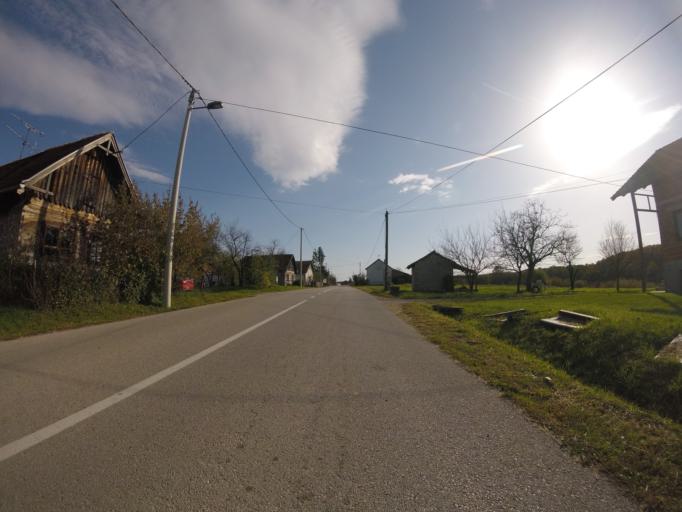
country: HR
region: Zagrebacka
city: Mraclin
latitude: 45.6327
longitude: 16.0632
